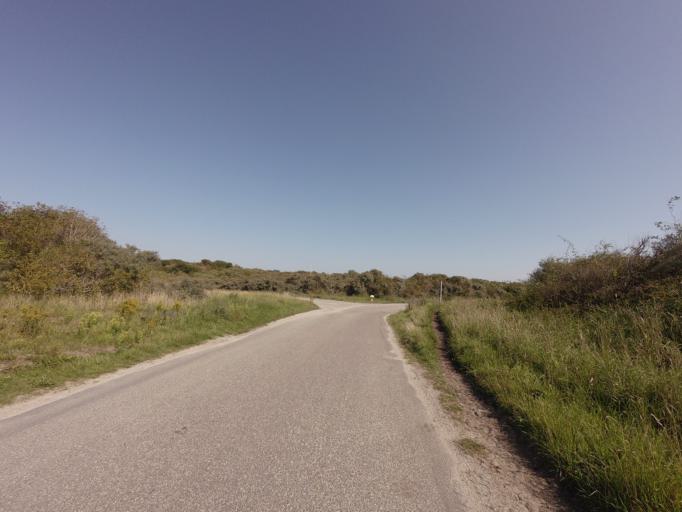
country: NL
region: Friesland
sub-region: Gemeente Schiermonnikoog
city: Schiermonnikoog
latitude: 53.4958
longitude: 6.1858
